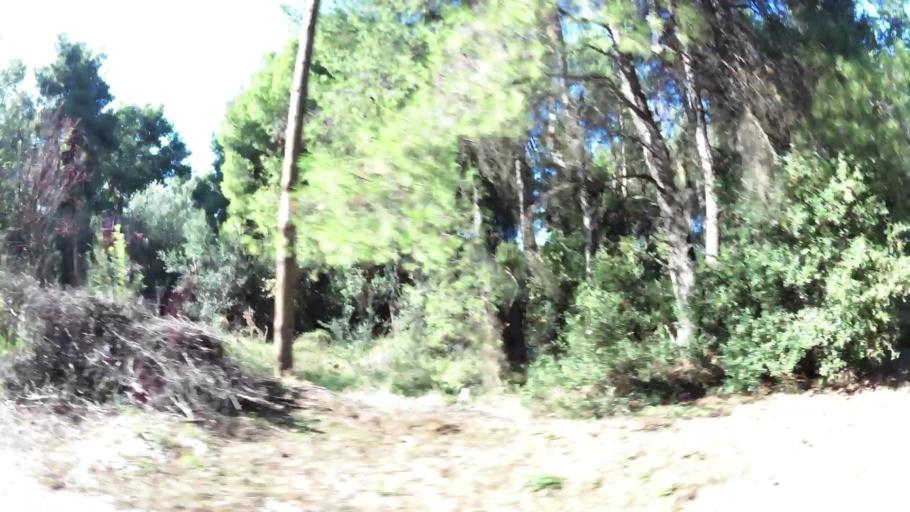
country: GR
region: Attica
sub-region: Nomarchia Anatolikis Attikis
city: Drosia
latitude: 38.1107
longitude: 23.8584
